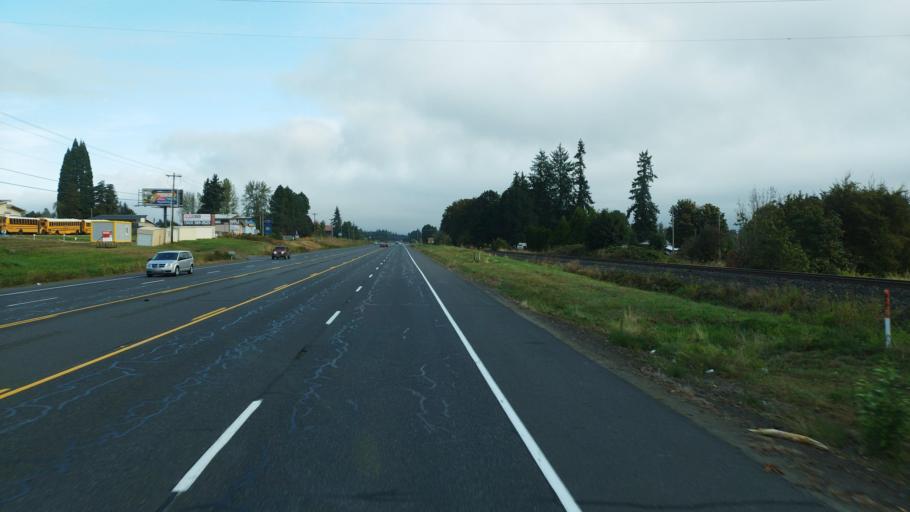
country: US
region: Oregon
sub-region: Columbia County
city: Scappoose
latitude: 45.7754
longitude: -122.8776
